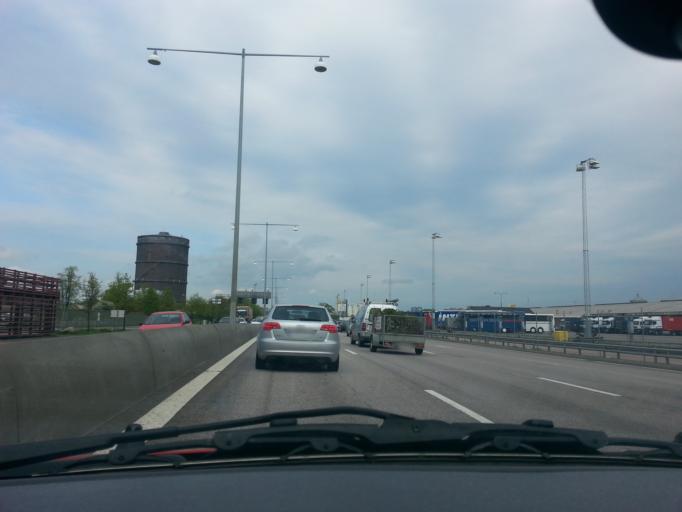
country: SE
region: Vaestra Goetaland
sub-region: Goteborg
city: Goeteborg
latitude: 57.7142
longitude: 11.9756
